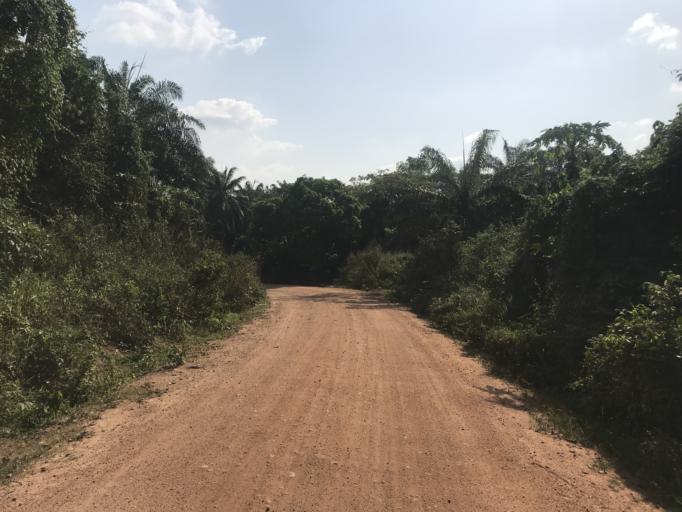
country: NG
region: Osun
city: Ikirun
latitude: 7.8716
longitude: 4.5851
